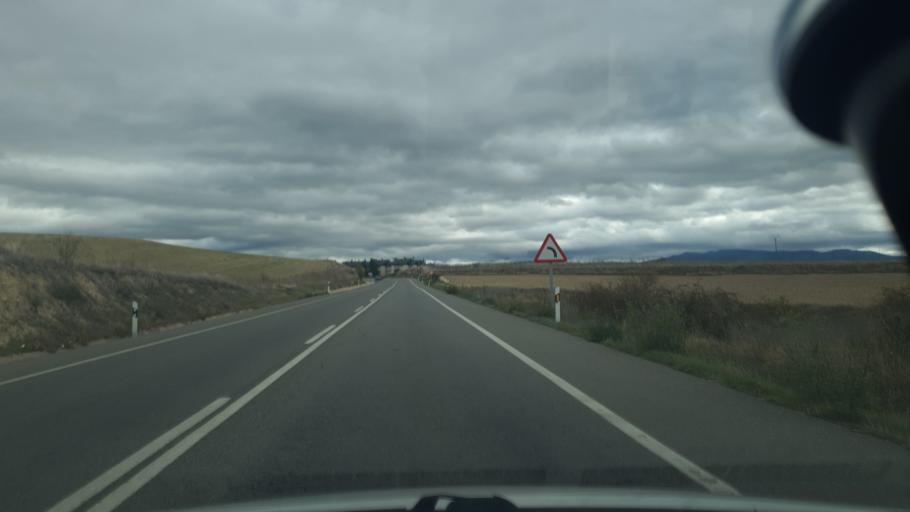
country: ES
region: Castille and Leon
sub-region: Provincia de Segovia
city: Segovia
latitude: 40.9432
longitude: -4.1419
